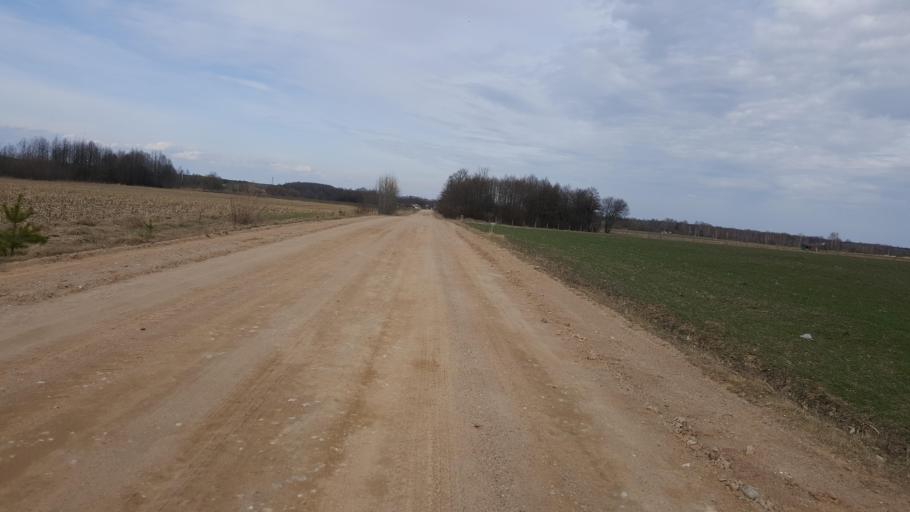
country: BY
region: Brest
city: Kamyanyets
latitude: 52.3838
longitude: 23.9948
